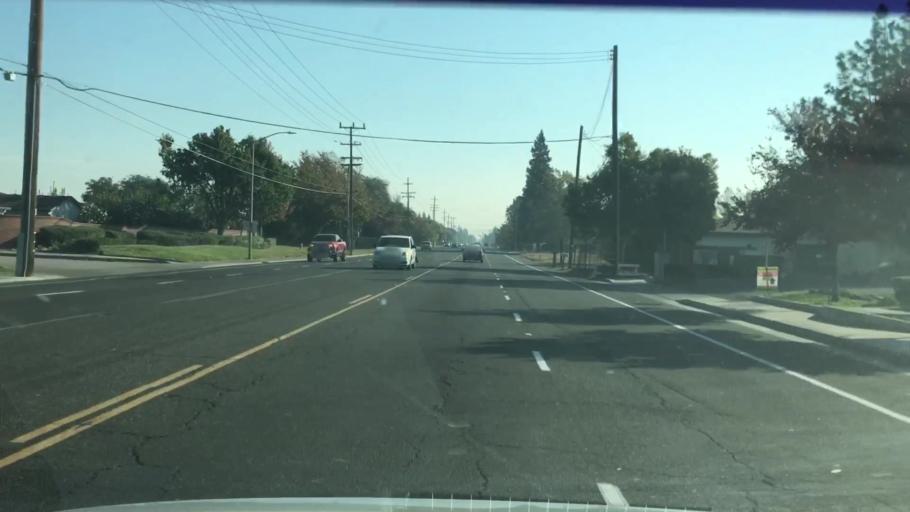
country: US
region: California
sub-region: Sacramento County
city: Florin
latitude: 38.4743
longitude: -121.4162
